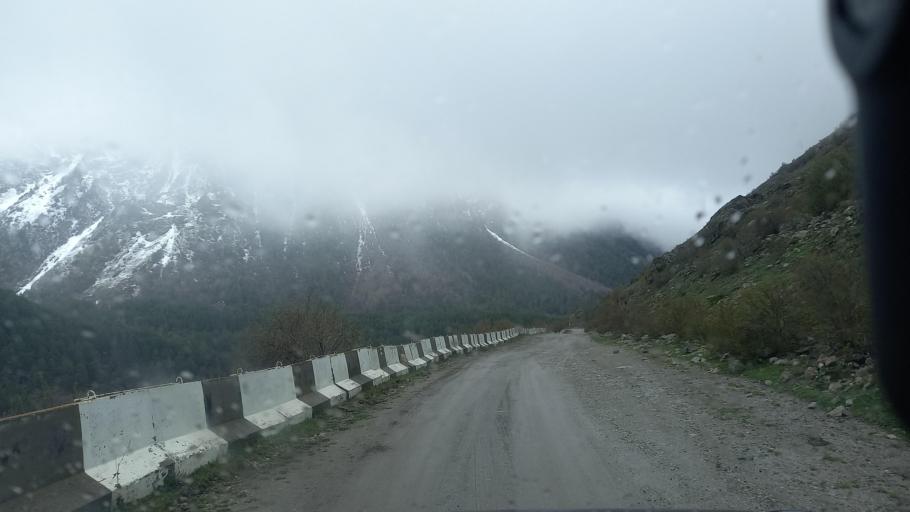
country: RU
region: Kabardino-Balkariya
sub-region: El'brusskiy Rayon
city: El'brus
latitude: 43.2263
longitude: 42.6665
